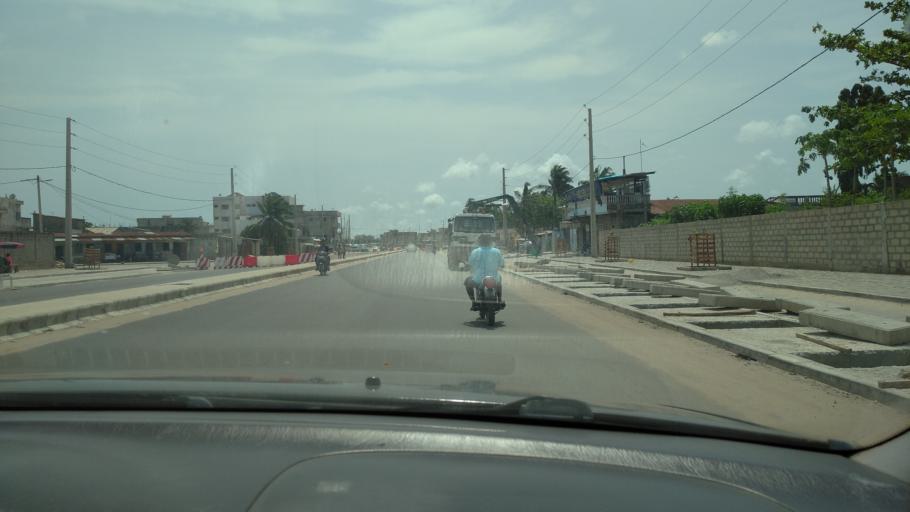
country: BJ
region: Littoral
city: Cotonou
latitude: 6.3744
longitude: 2.4960
